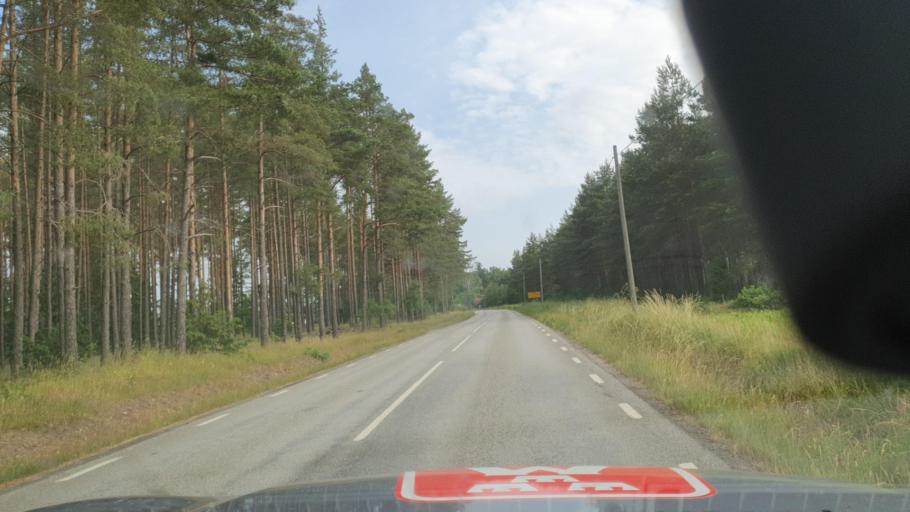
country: SE
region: Kalmar
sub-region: Kalmar Kommun
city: Trekanten
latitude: 56.6341
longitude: 16.0307
